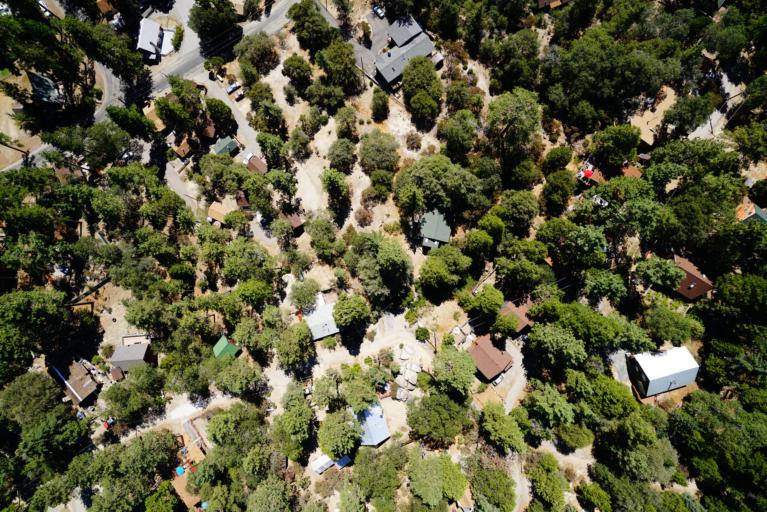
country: US
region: California
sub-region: Riverside County
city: Idyllwild-Pine Cove
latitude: 33.7593
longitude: -116.7417
